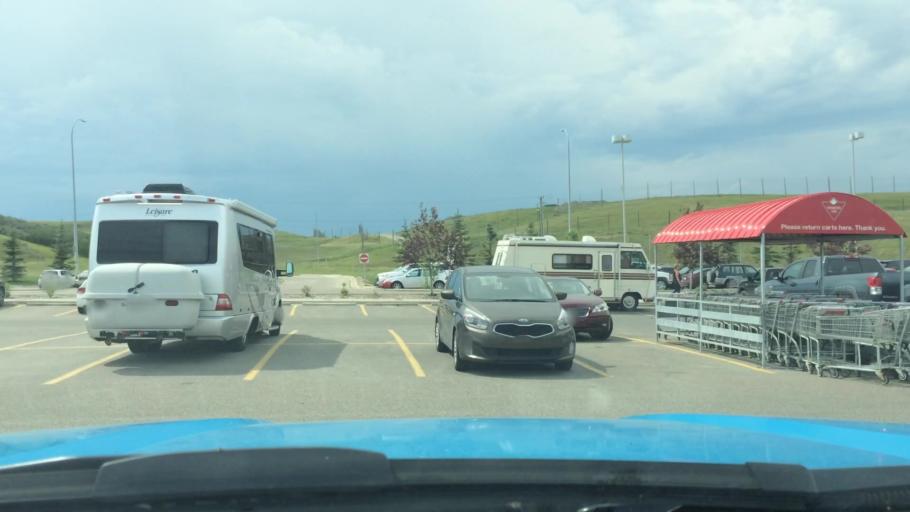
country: CA
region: Alberta
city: Calgary
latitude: 51.1587
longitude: -114.1610
